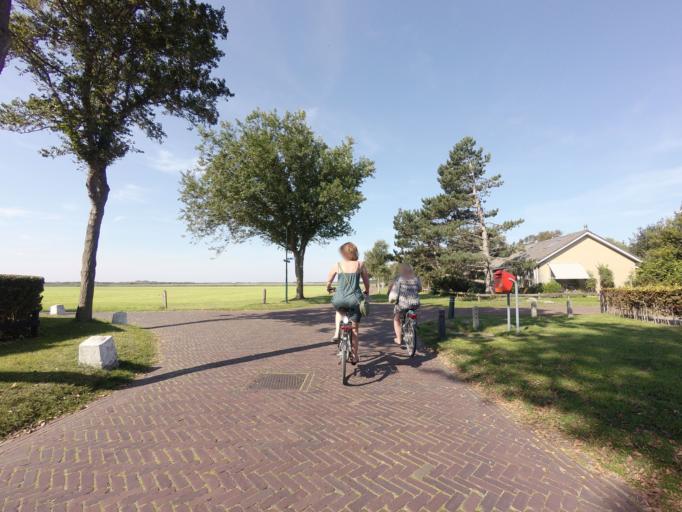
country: NL
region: Friesland
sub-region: Gemeente Schiermonnikoog
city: Schiermonnikoog
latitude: 53.4780
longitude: 6.1547
